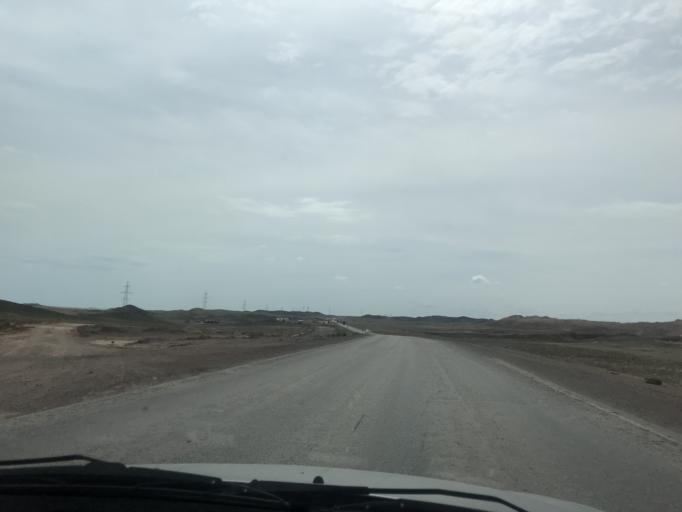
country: KZ
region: Zhambyl
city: Mynaral
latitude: 45.3684
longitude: 73.6605
